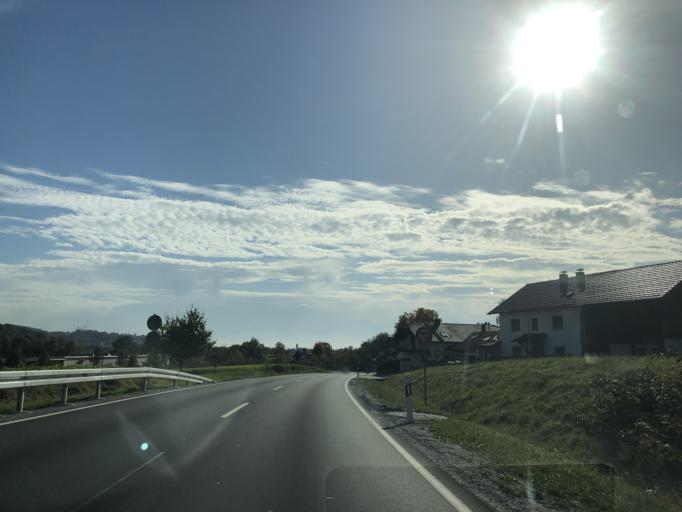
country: DE
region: Bavaria
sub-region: Lower Bavaria
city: Deggendorf
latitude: 48.8650
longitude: 12.9589
